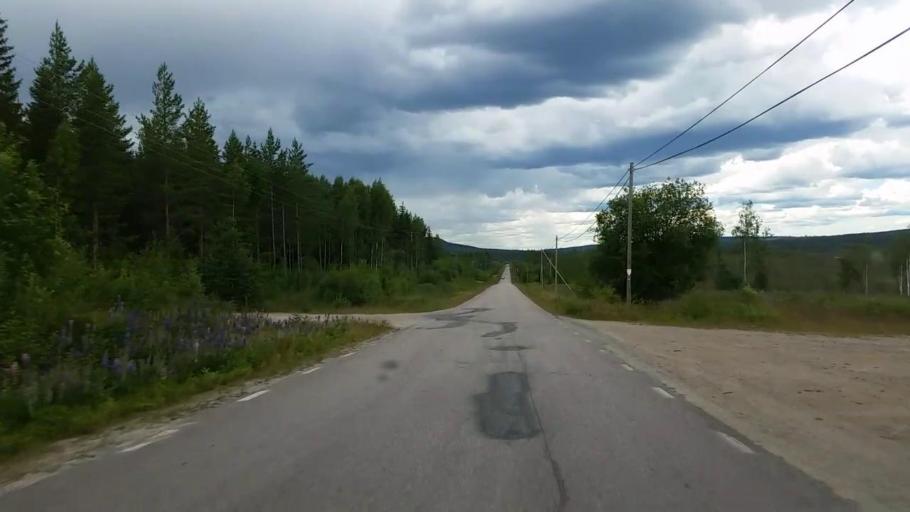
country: SE
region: Gaevleborg
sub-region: Ovanakers Kommun
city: Edsbyn
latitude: 61.4377
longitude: 15.8936
